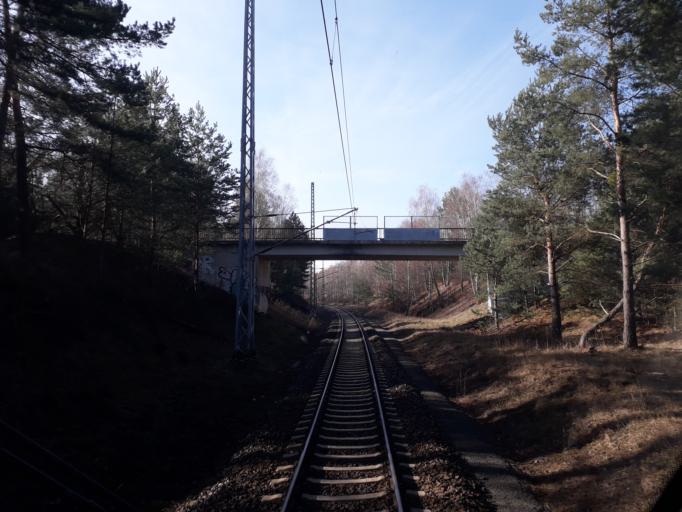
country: DE
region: Brandenburg
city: Beelitz
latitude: 52.2892
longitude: 12.9547
